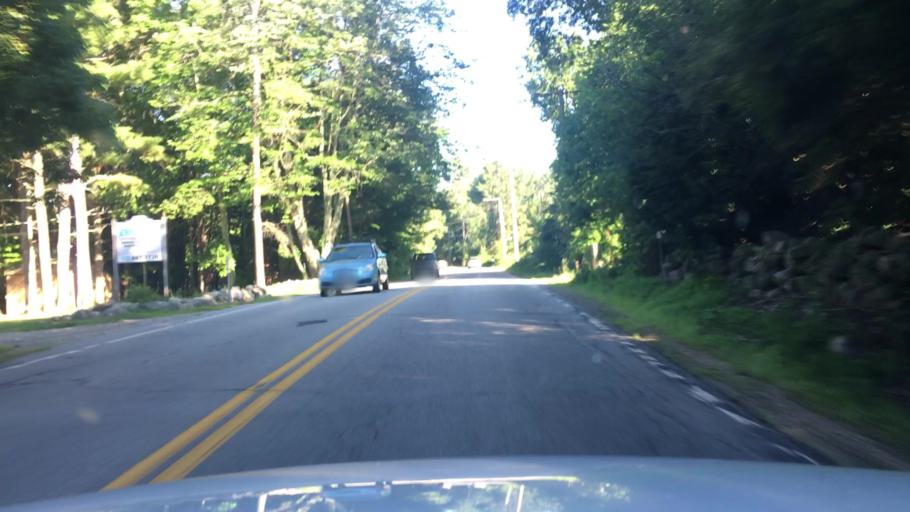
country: US
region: New Hampshire
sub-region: Rockingham County
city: Sandown
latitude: 42.9118
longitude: -71.1615
